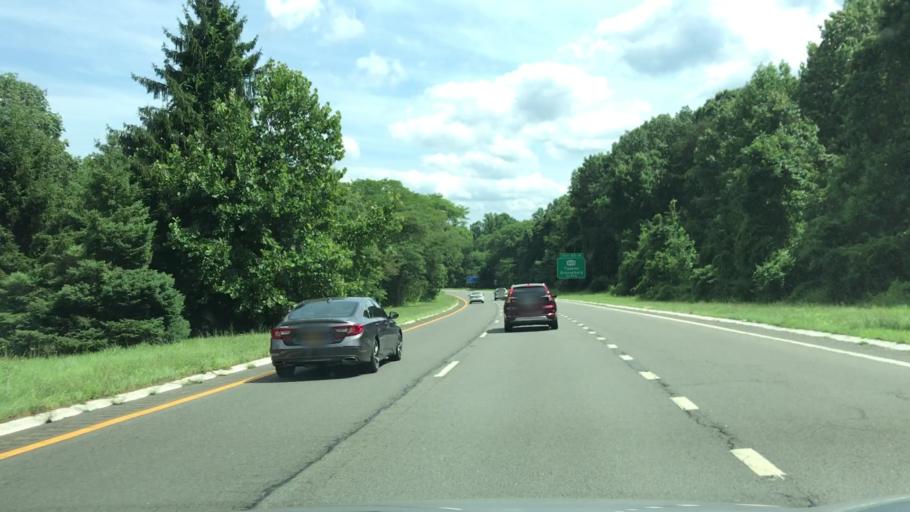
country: US
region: New York
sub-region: Rockland County
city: Orangeburg
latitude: 41.0421
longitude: -73.9564
